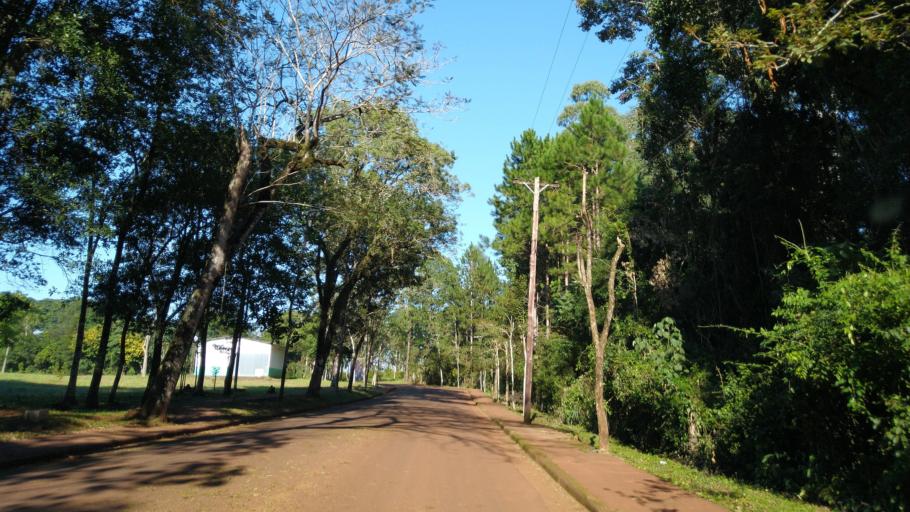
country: AR
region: Misiones
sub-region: Departamento de Montecarlo
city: Montecarlo
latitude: -26.5563
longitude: -54.7735
